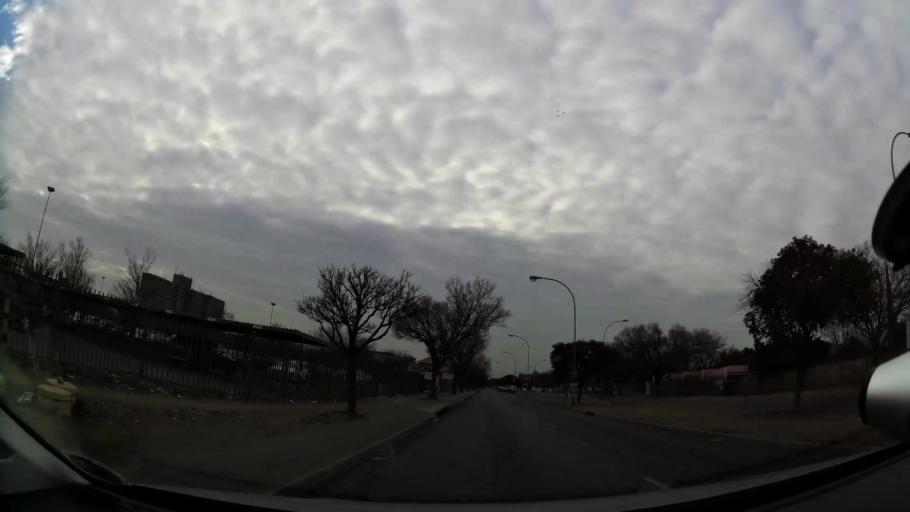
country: ZA
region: Orange Free State
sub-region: Mangaung Metropolitan Municipality
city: Bloemfontein
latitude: -29.1187
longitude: 26.1842
